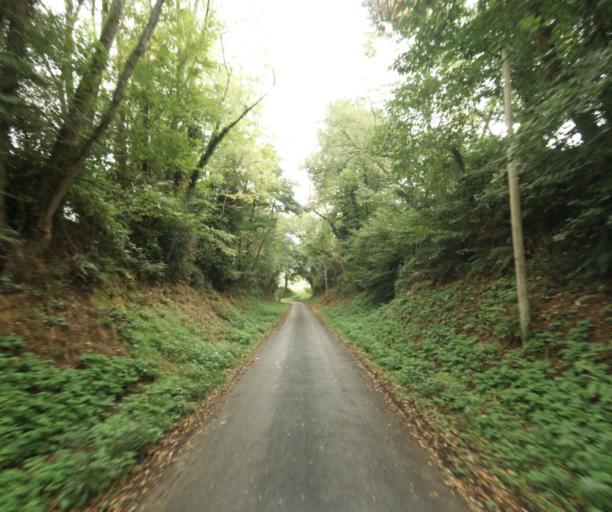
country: FR
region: Midi-Pyrenees
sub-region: Departement du Gers
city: Nogaro
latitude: 43.8222
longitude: -0.0863
